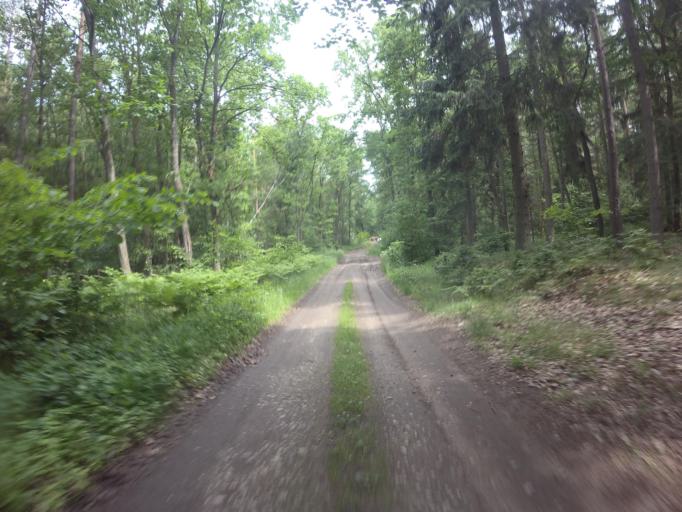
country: PL
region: West Pomeranian Voivodeship
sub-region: Powiat choszczenski
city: Recz
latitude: 53.3174
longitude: 15.5275
